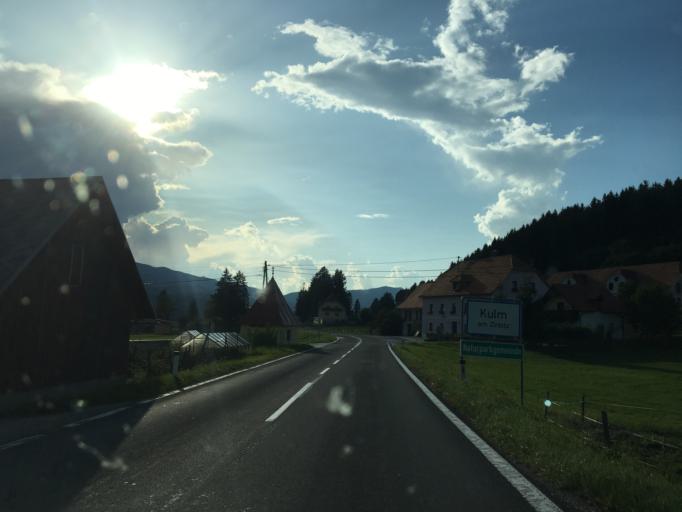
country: AT
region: Styria
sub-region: Politischer Bezirk Murau
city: Kulm am Zirbitz
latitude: 47.0488
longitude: 14.4619
